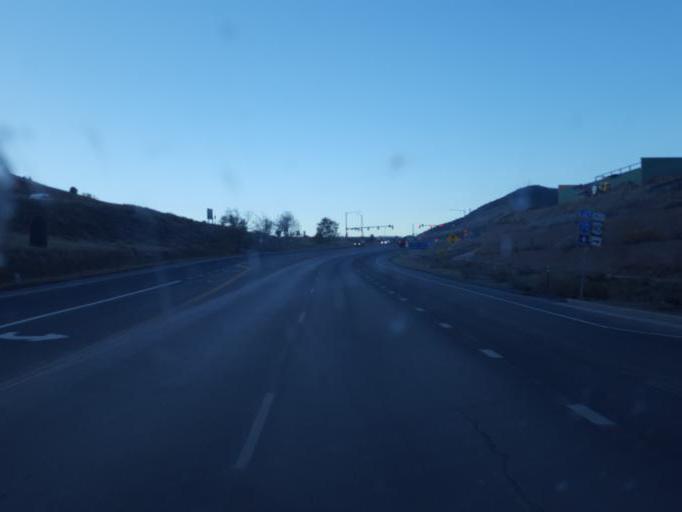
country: US
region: Colorado
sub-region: Jefferson County
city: West Pleasant View
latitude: 39.7041
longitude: -105.2039
